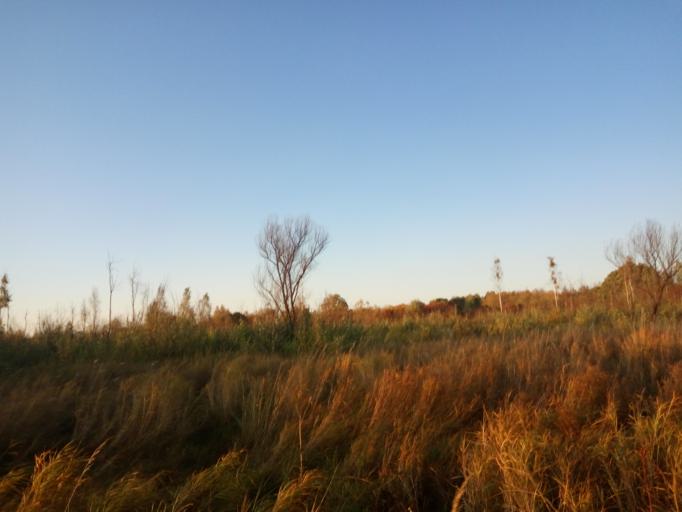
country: RU
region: Khabarovsk Krai
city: Khor
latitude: 47.7036
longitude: 134.9643
